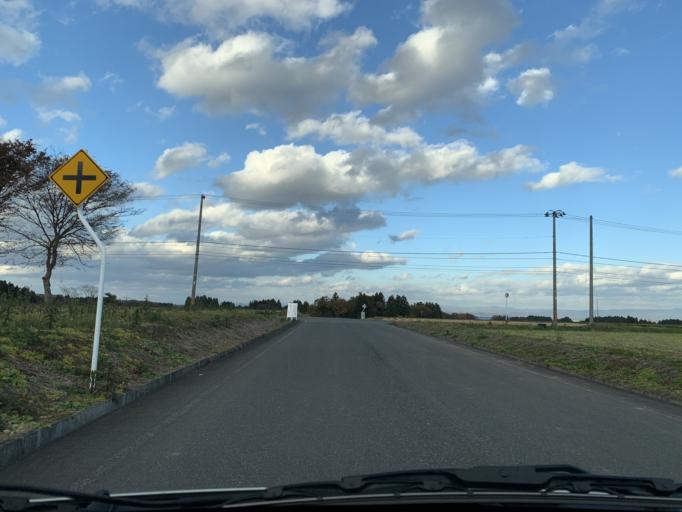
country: JP
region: Iwate
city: Mizusawa
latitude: 39.1069
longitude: 141.0229
